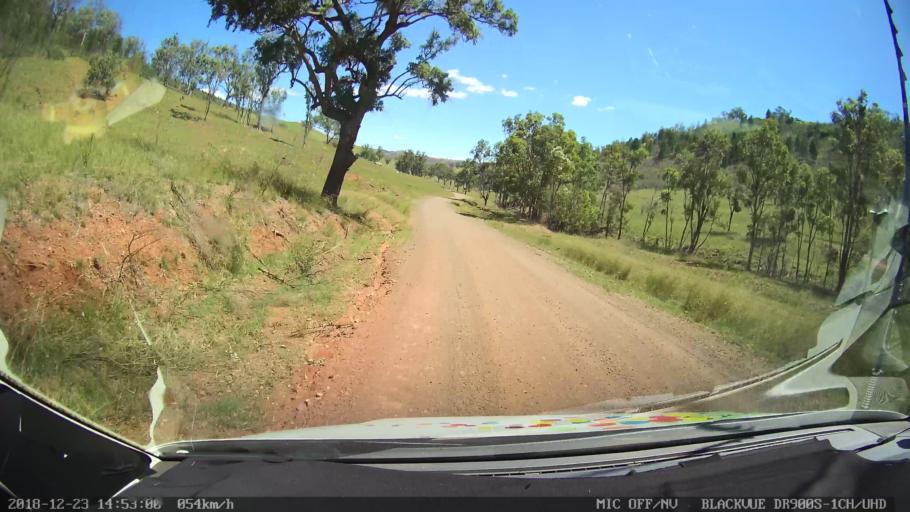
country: AU
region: New South Wales
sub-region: Tamworth Municipality
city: Manilla
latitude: -30.6882
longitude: 150.8523
